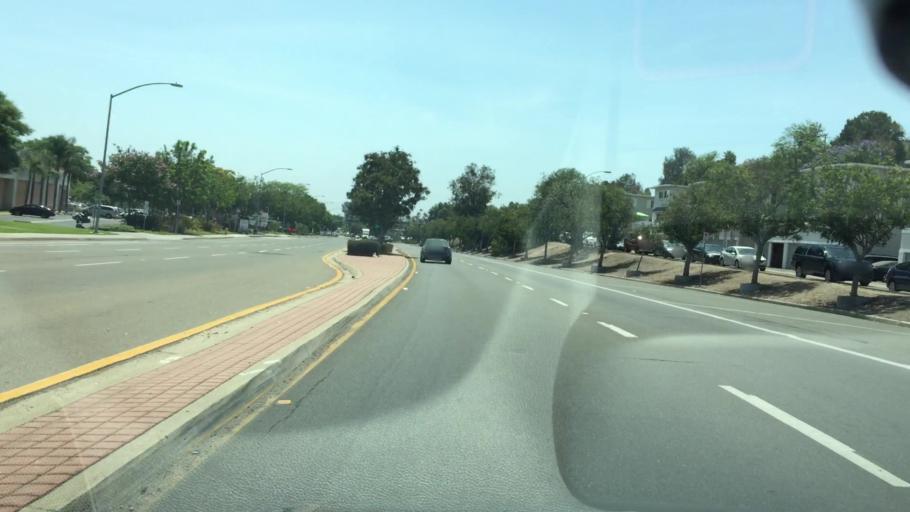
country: US
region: California
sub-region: San Diego County
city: Lemon Grove
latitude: 32.7520
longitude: -117.0675
